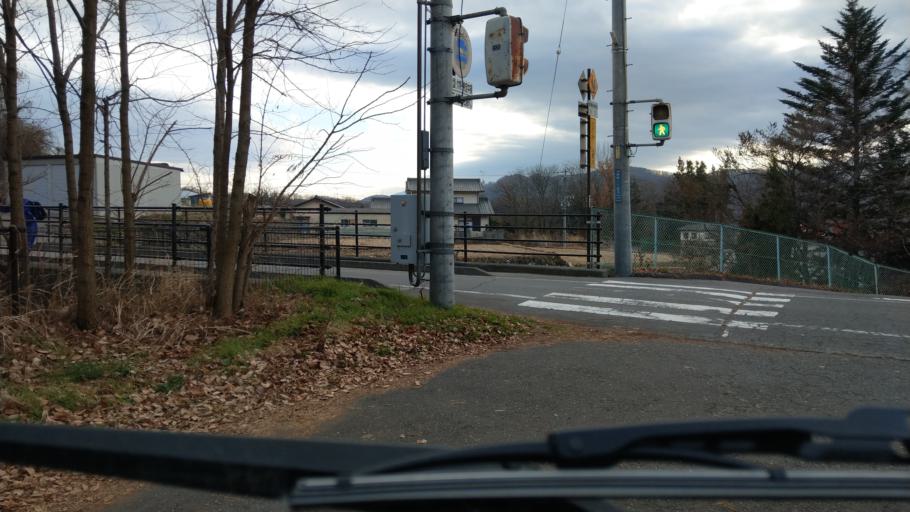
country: JP
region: Nagano
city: Komoro
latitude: 36.3332
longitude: 138.4167
